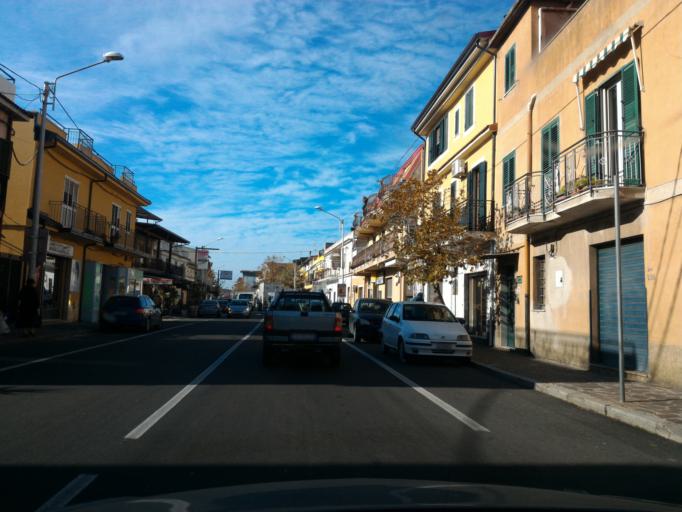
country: IT
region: Calabria
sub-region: Provincia di Catanzaro
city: Botricello
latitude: 38.9359
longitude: 16.8592
